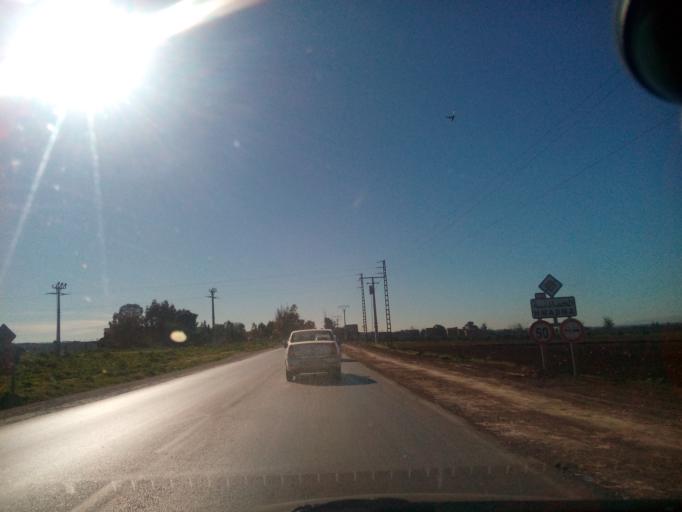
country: DZ
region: Relizane
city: Djidiouia
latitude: 35.9136
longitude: 0.7843
